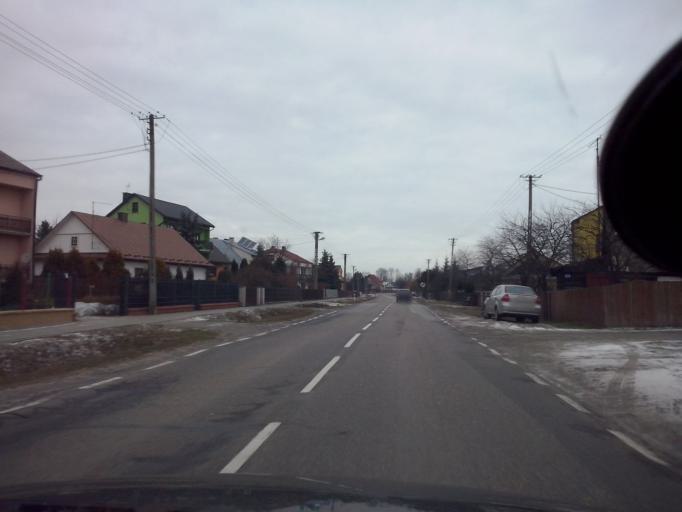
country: PL
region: Lublin Voivodeship
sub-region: Powiat bilgorajski
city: Bilgoraj
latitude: 50.5052
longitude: 22.6456
